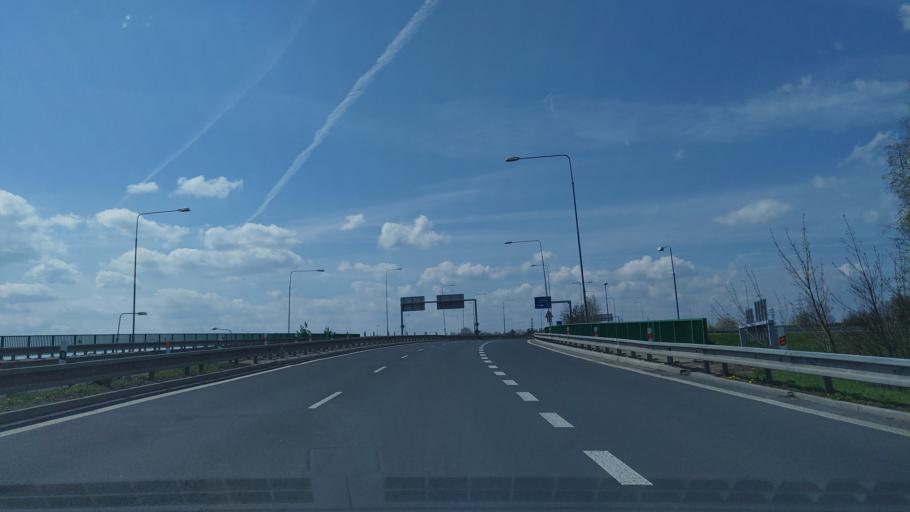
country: CZ
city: Krasna Lipa
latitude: 50.4555
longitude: 13.3766
